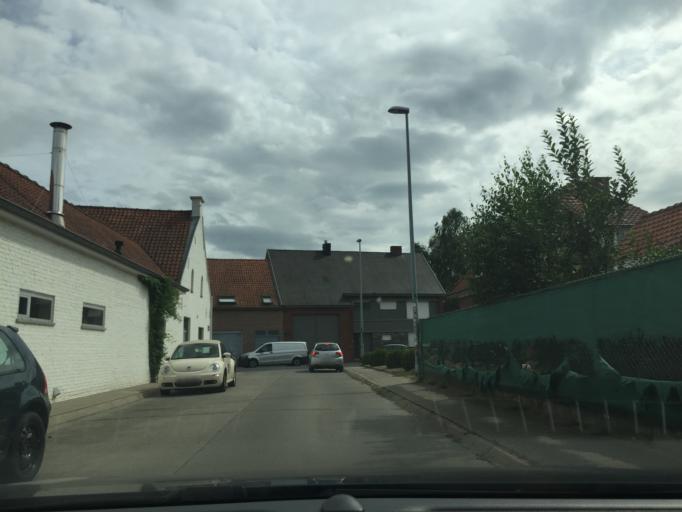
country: BE
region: Flanders
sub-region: Provincie West-Vlaanderen
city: Izegem
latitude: 50.9331
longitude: 3.1945
